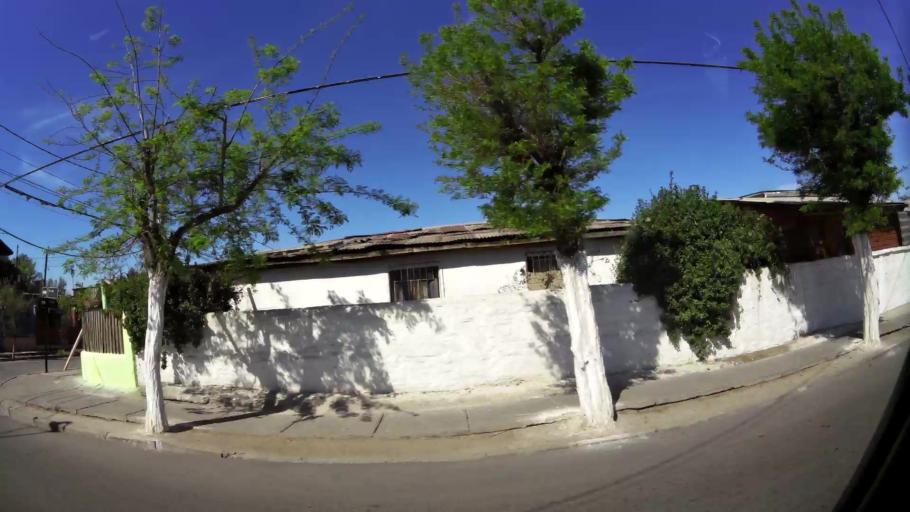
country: CL
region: Santiago Metropolitan
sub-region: Provincia de Santiago
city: Lo Prado
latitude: -33.4999
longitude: -70.7192
